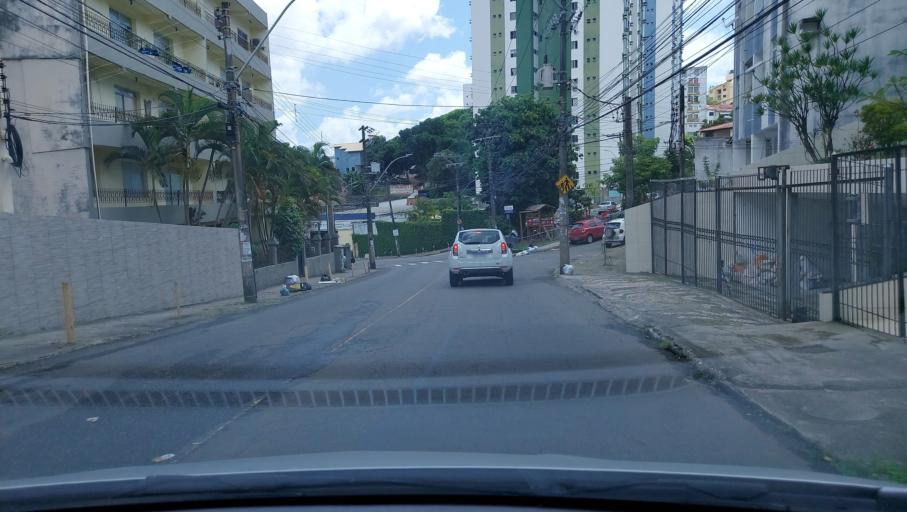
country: BR
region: Bahia
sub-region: Salvador
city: Salvador
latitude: -12.9693
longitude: -38.4885
